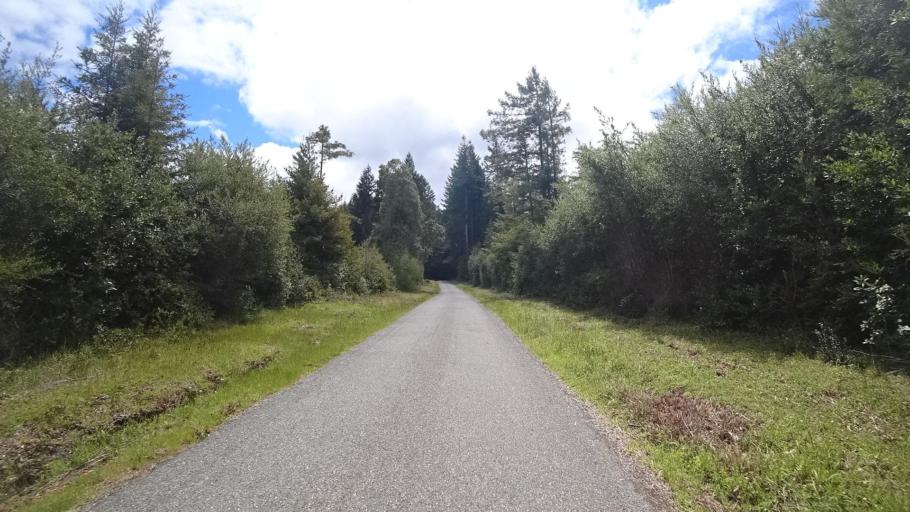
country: US
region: California
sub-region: Humboldt County
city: Blue Lake
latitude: 40.7857
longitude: -123.9650
